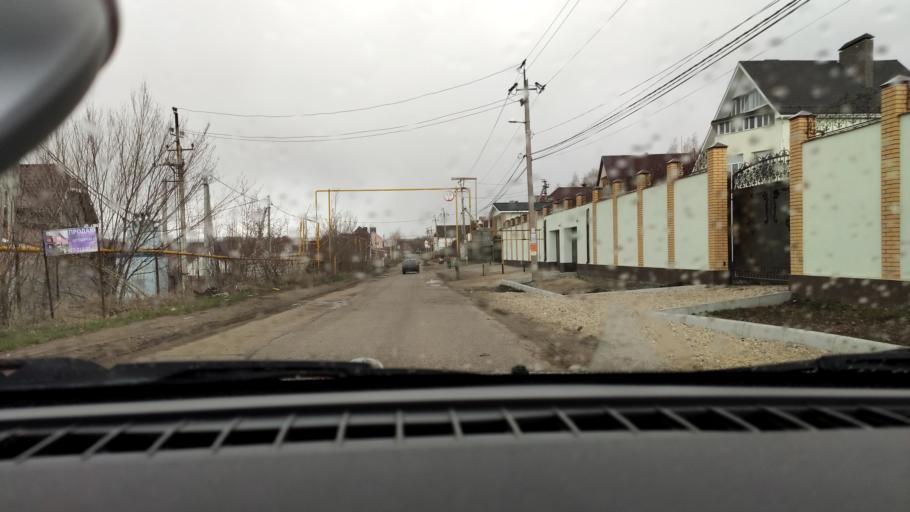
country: RU
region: Samara
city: Novosemeykino
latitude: 53.3266
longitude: 50.2906
